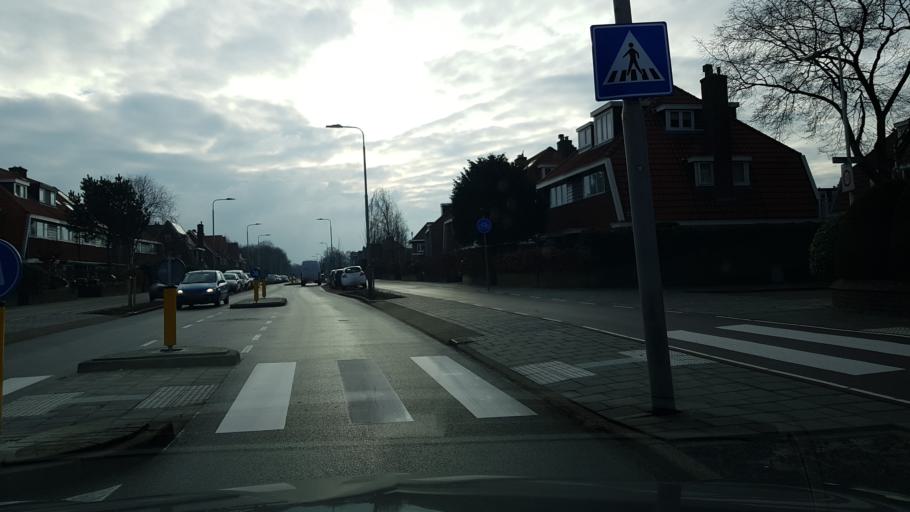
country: NL
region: North Holland
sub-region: Gemeente Velsen
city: Velsen-Zuid
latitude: 52.4482
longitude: 4.6385
